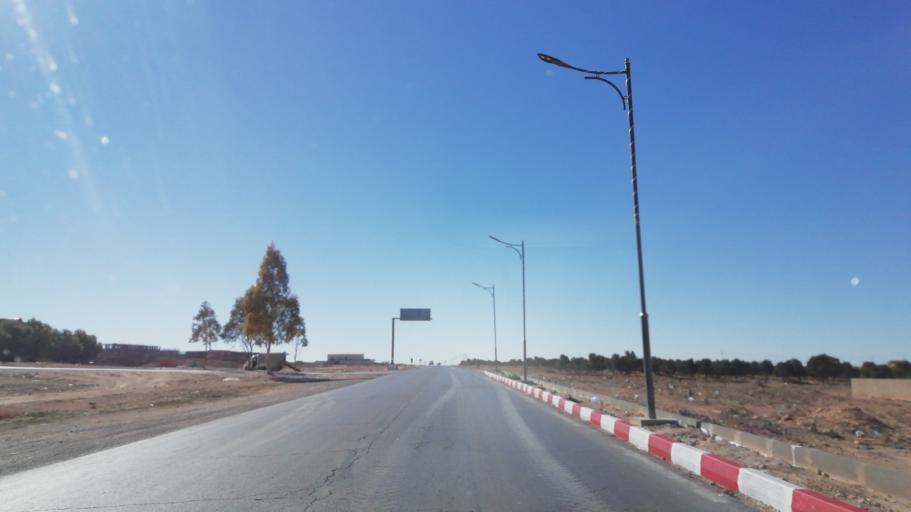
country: DZ
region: Saida
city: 'Ain el Hadjar
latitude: 34.0356
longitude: 0.0775
